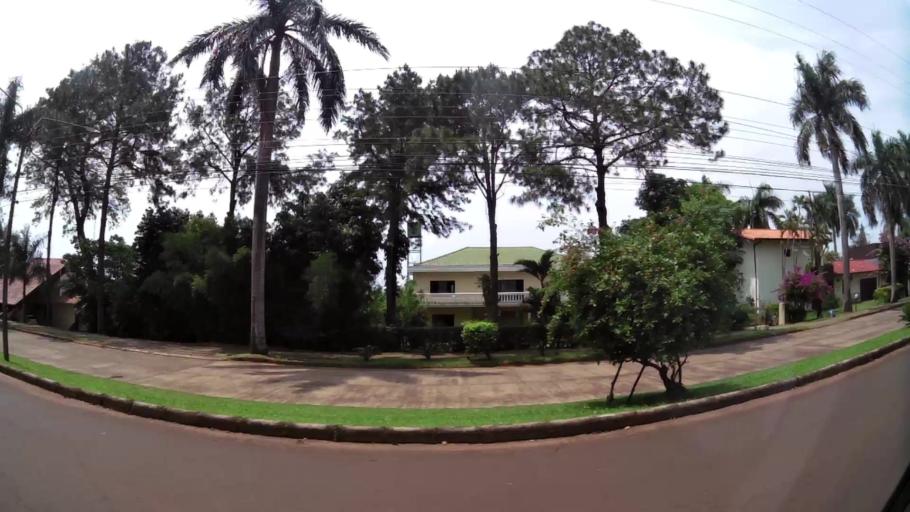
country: PY
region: Alto Parana
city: Ciudad del Este
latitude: -25.4839
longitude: -54.6180
